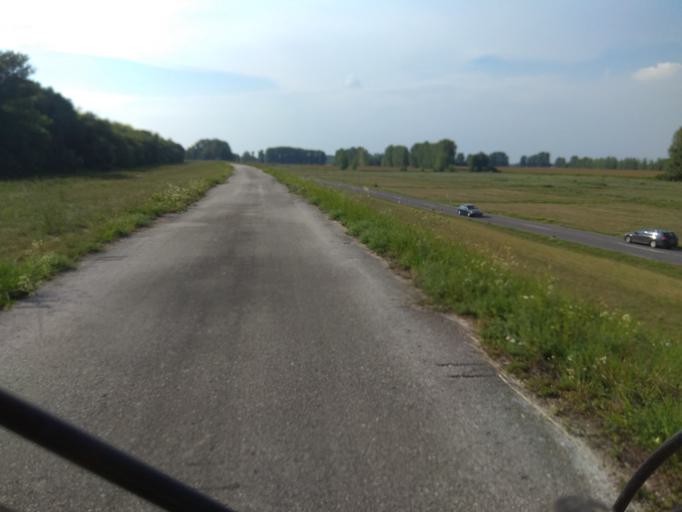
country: SK
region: Trnavsky
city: Gabcikovo
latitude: 47.8048
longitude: 17.6452
